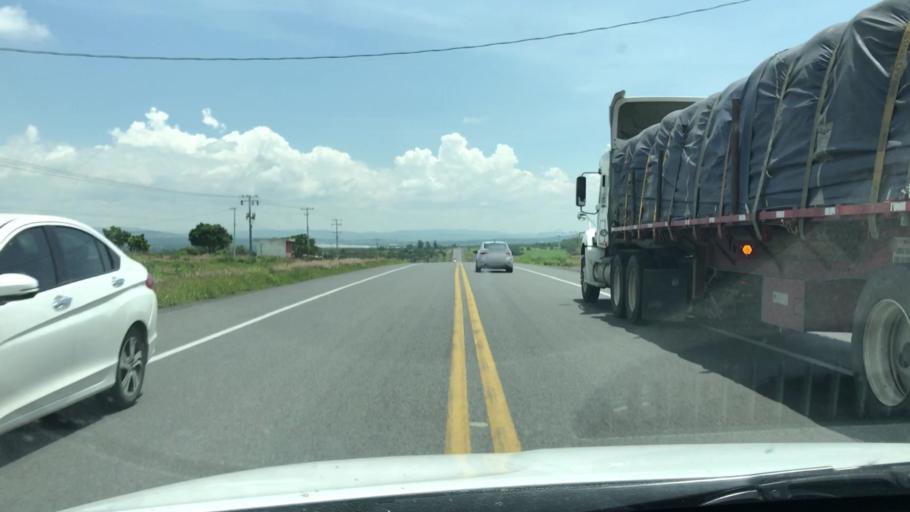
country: MX
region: Jalisco
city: Degollado
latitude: 20.3492
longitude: -102.1570
